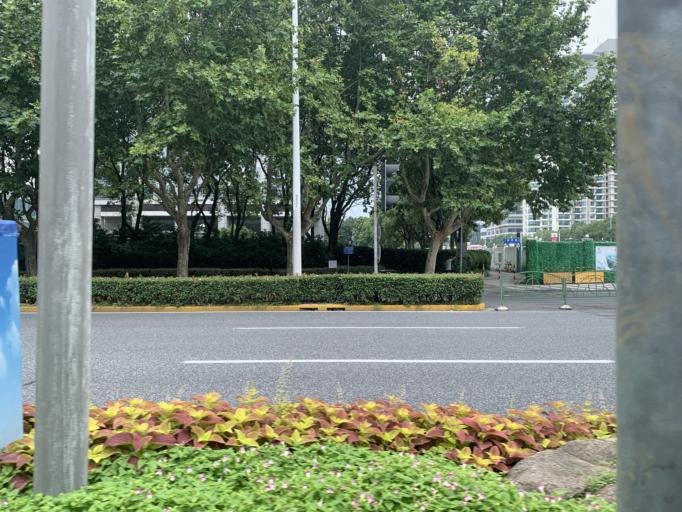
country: CN
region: Shanghai Shi
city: Huamu
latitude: 31.2219
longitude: 121.5468
